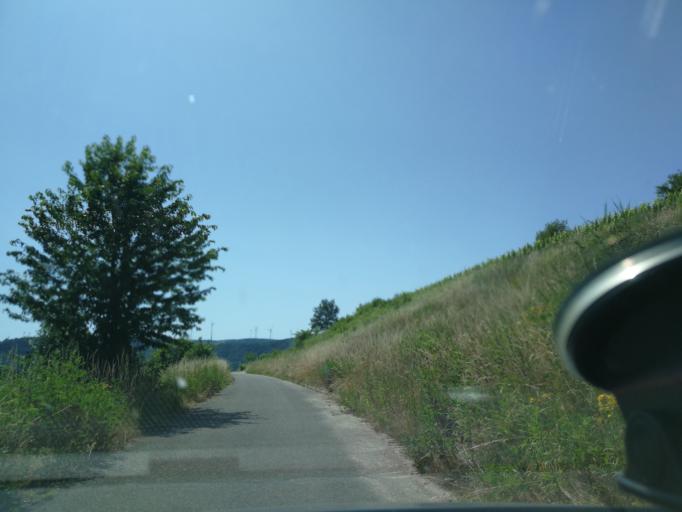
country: DE
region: Rheinland-Pfalz
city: Wintrich
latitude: 49.8805
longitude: 6.9386
